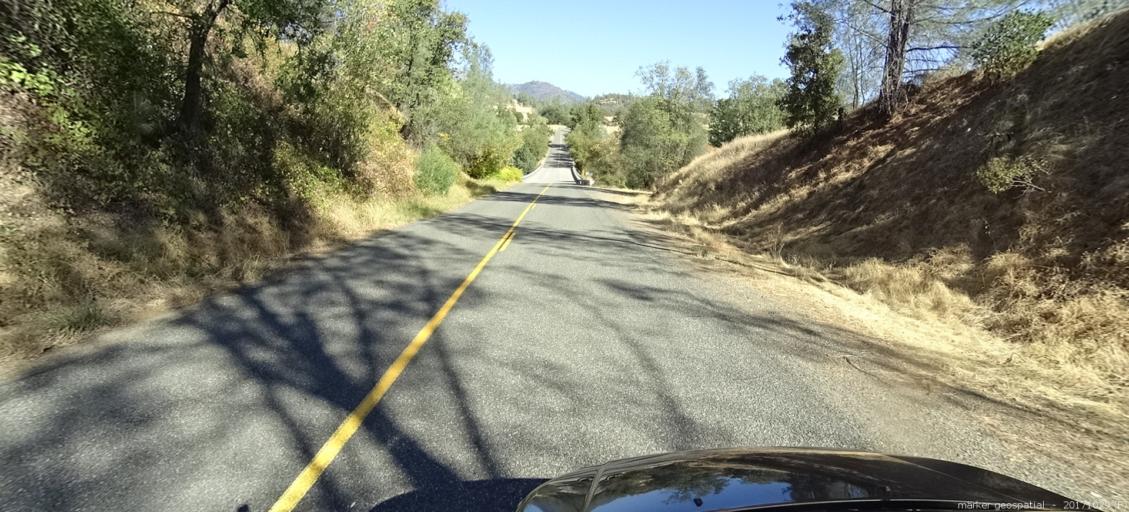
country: US
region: California
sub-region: Shasta County
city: Shasta
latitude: 40.4691
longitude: -122.6228
